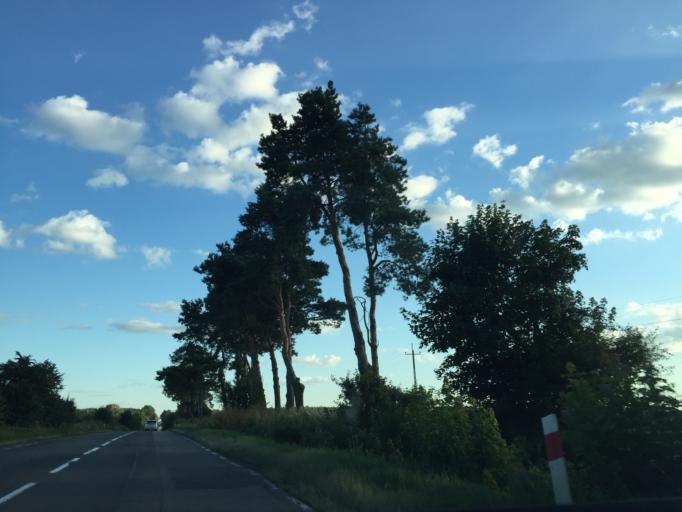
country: PL
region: Podlasie
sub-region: Powiat lomzynski
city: Sniadowo
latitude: 53.0982
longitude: 22.0249
